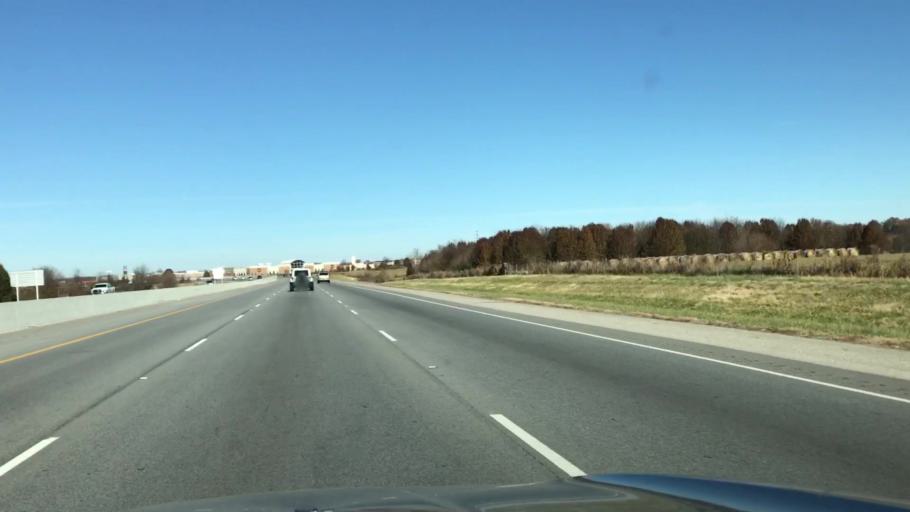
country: US
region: Arkansas
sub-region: Benton County
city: Lowell
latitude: 36.2694
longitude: -94.1502
